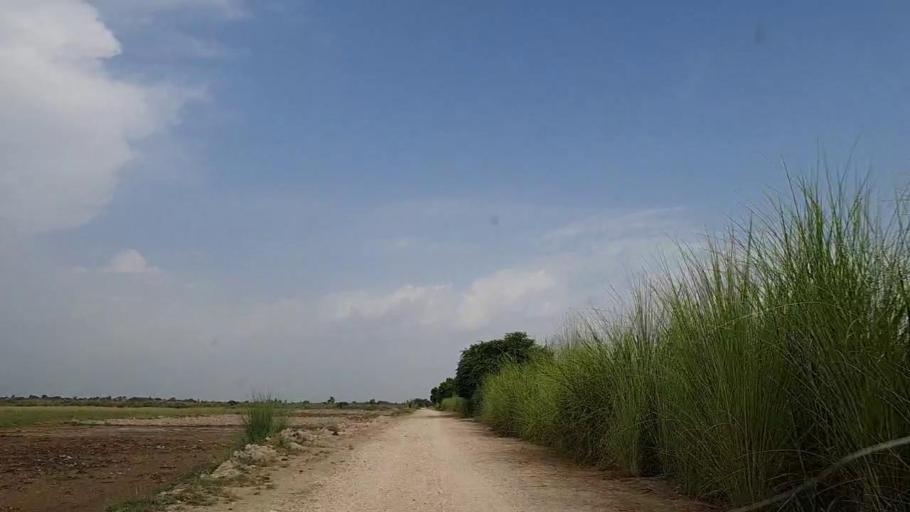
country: PK
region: Sindh
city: Khanpur
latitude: 27.8238
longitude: 69.5212
